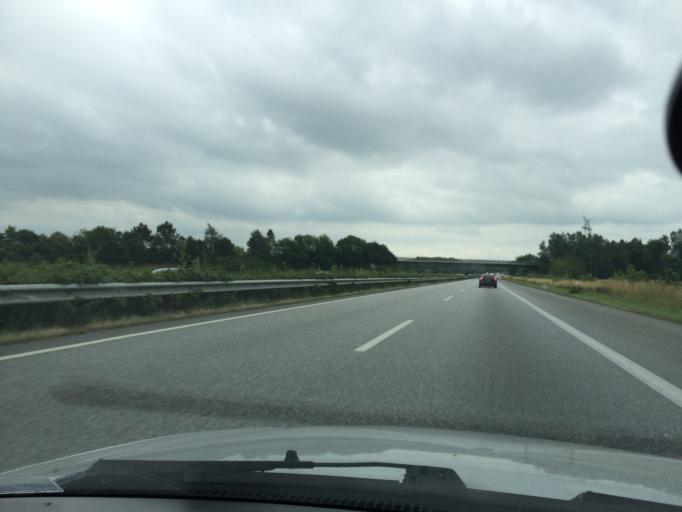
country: DE
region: Schleswig-Holstein
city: Tarp
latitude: 54.6805
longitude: 9.4189
